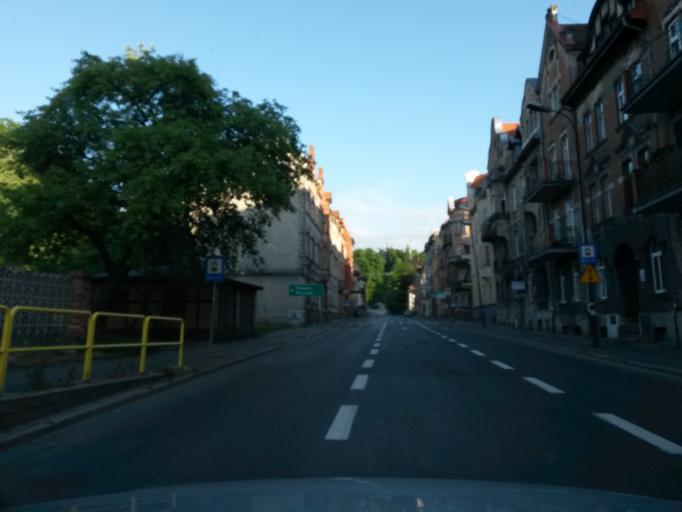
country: PL
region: Lower Silesian Voivodeship
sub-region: Jelenia Gora
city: Jelenia Gora
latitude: 50.8999
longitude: 15.7366
